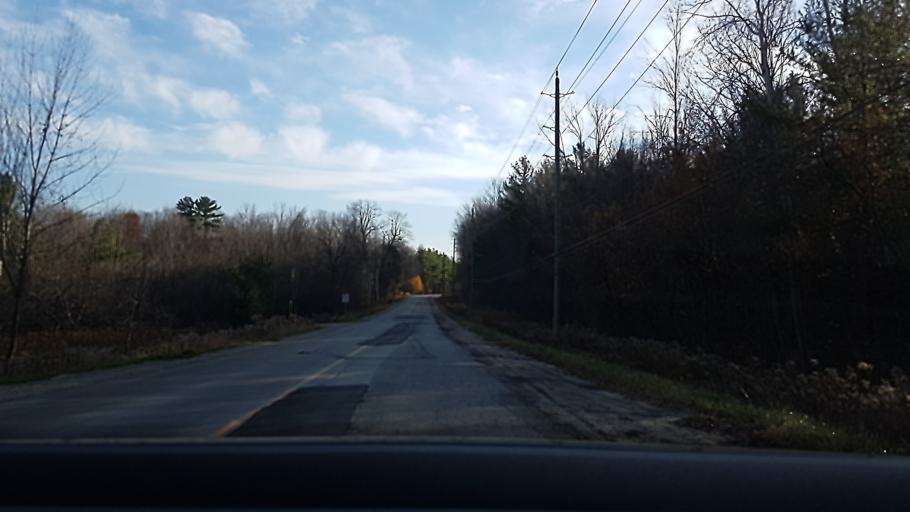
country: CA
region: Ontario
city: Barrie
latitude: 44.3748
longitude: -79.5527
